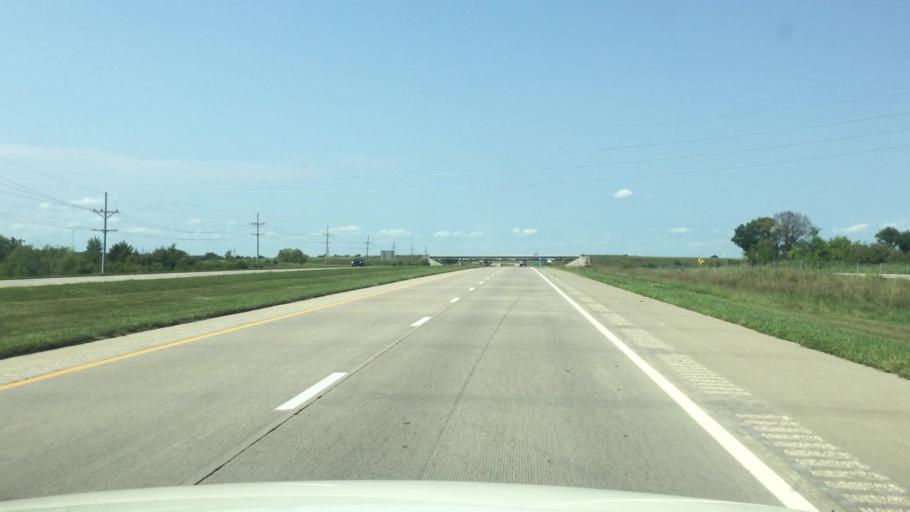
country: US
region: Kansas
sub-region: Linn County
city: Pleasanton
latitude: 38.1622
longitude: -94.6957
